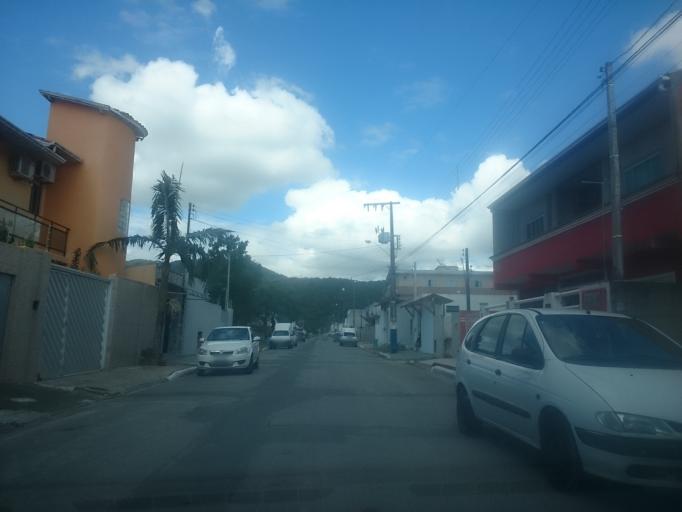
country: BR
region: Santa Catarina
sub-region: Balneario Camboriu
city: Balneario Camboriu
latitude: -27.0220
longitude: -48.6142
